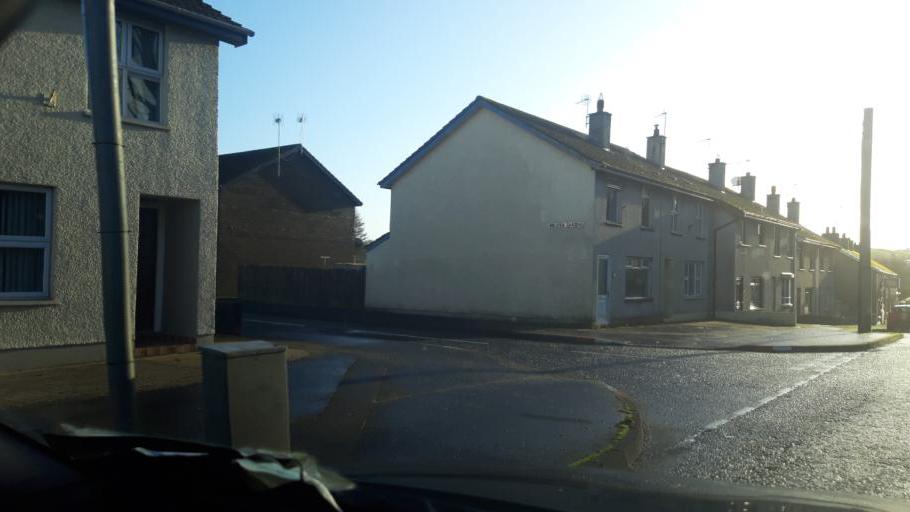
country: GB
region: Northern Ireland
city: Garvagh
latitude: 54.9815
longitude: -6.6880
